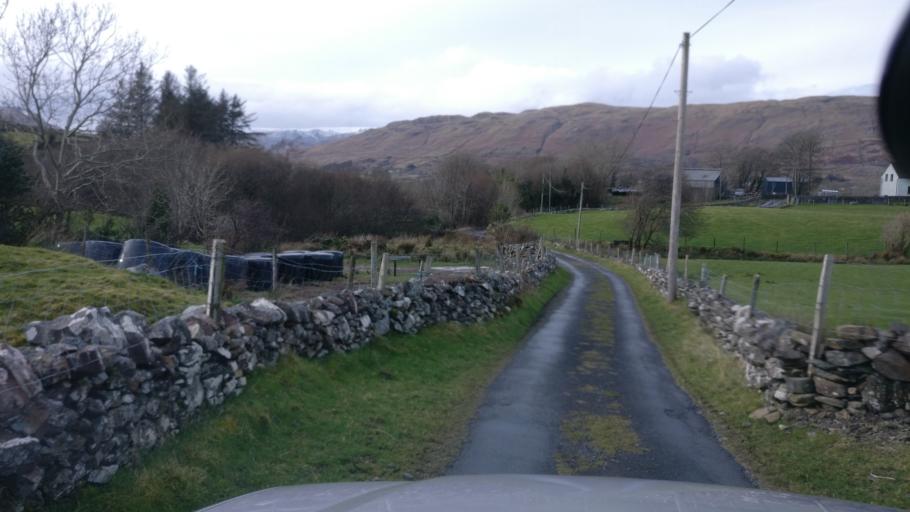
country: IE
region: Connaught
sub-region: County Galway
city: Oughterard
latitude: 53.5548
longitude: -9.4409
